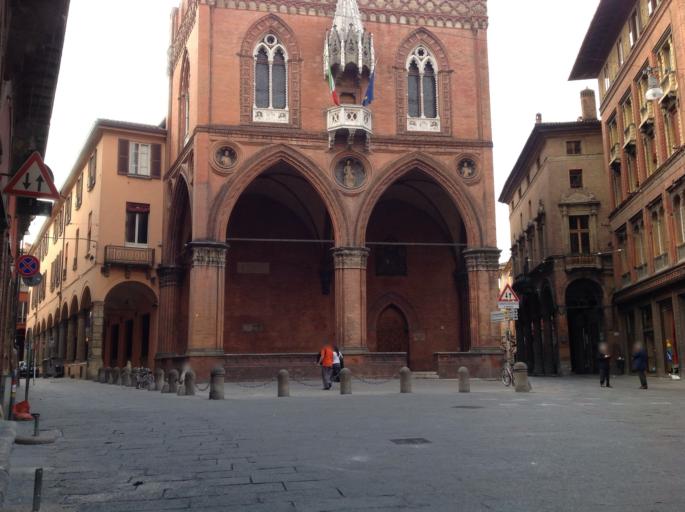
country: IT
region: Emilia-Romagna
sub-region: Provincia di Bologna
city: Bologna
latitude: 44.4938
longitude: 11.3463
